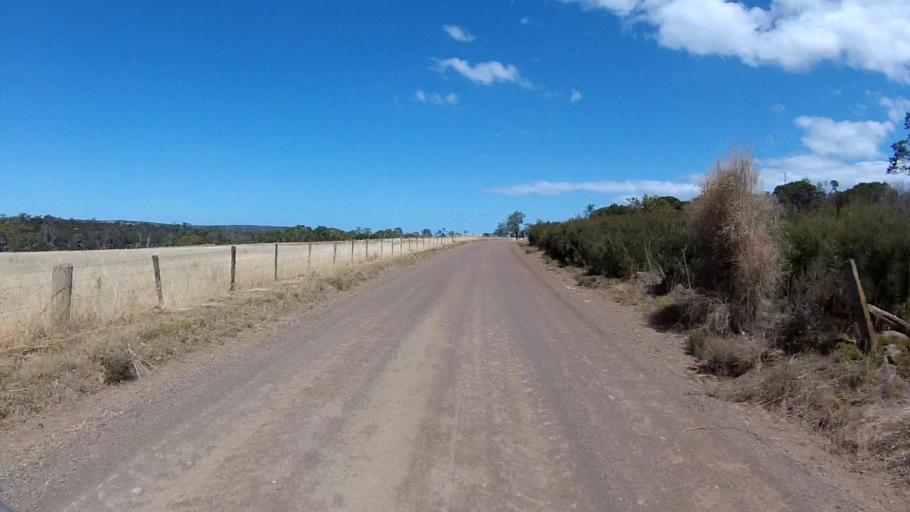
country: AU
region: Tasmania
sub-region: Break O'Day
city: St Helens
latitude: -41.9683
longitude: 148.0740
